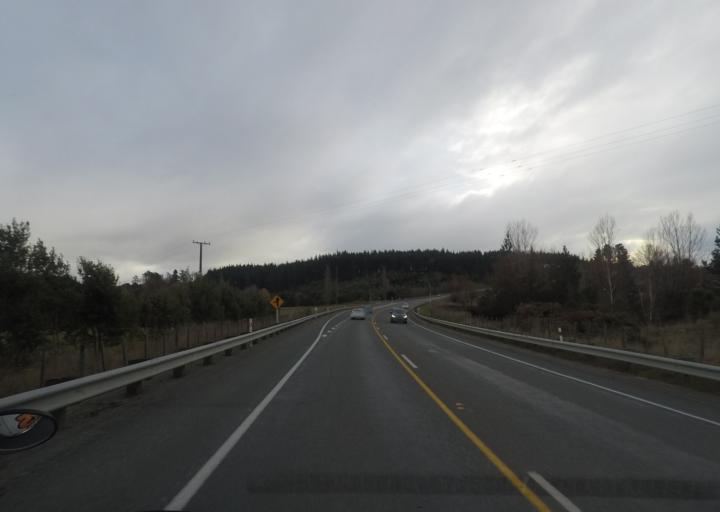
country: NZ
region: Tasman
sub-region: Tasman District
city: Mapua
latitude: -41.2801
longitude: 173.0705
